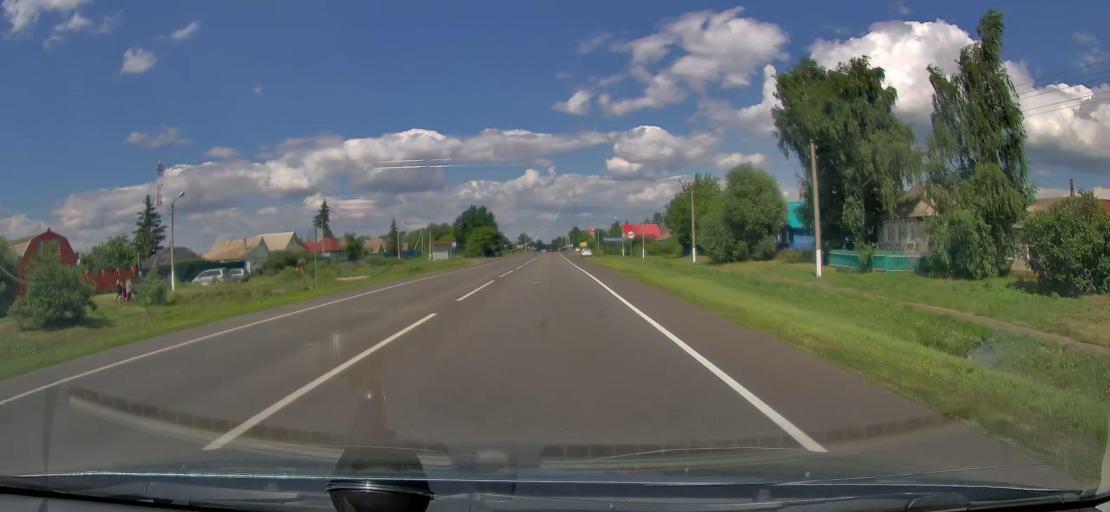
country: RU
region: Kursk
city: Zolotukhino
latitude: 51.9120
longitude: 36.3052
